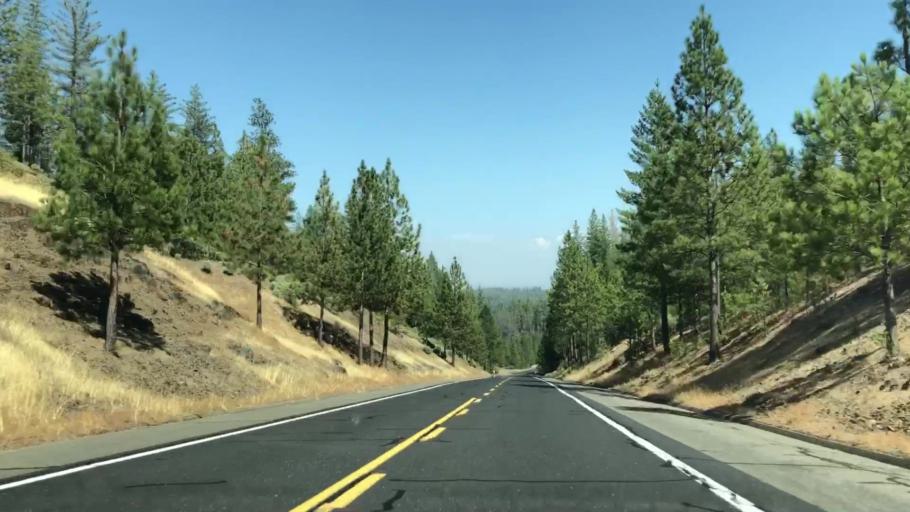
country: US
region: California
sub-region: Tuolumne County
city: Tuolumne City
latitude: 37.8207
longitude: -120.1549
